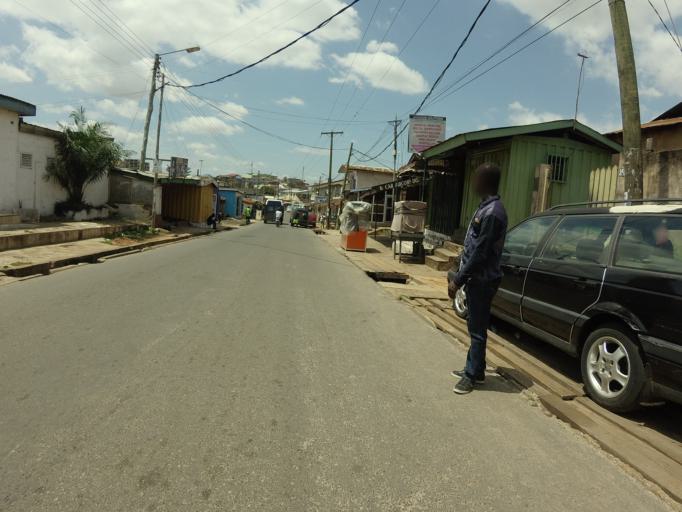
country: GH
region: Greater Accra
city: Accra
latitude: 5.5795
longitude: -0.2024
